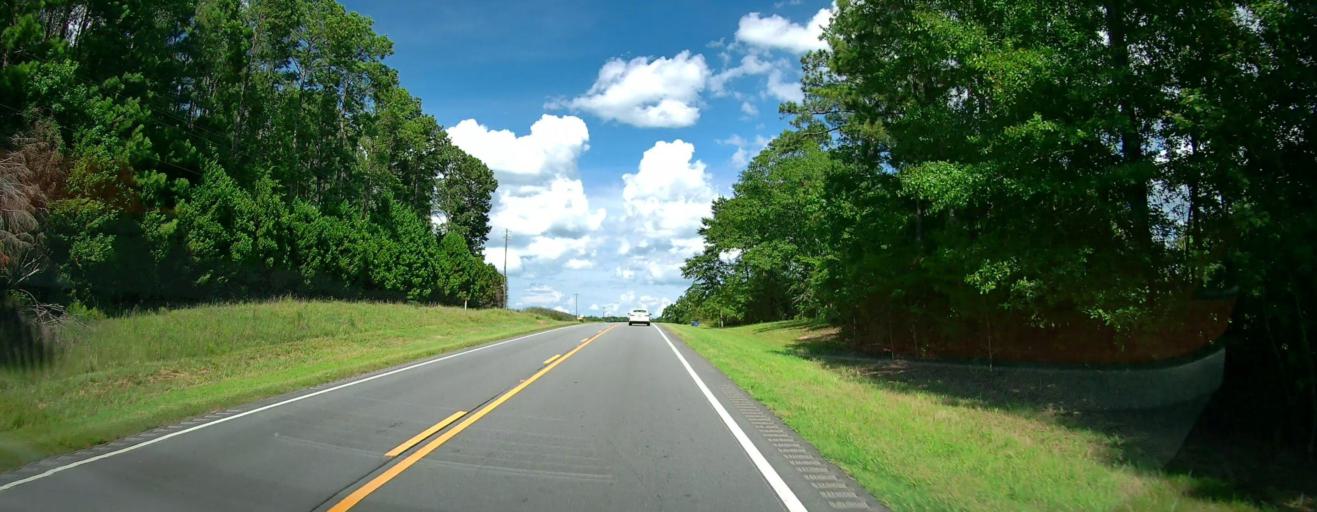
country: US
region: Alabama
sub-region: Lee County
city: Auburn
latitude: 32.4357
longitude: -85.4026
